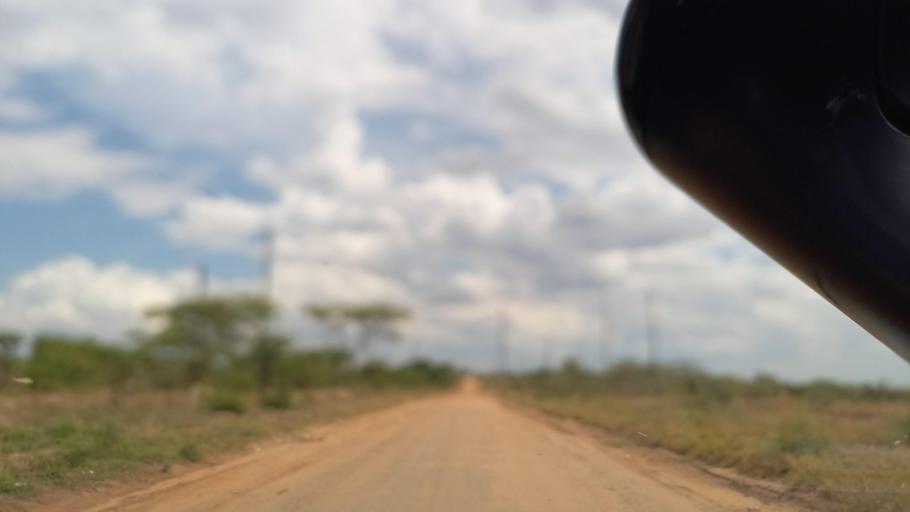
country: ZM
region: Southern
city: Nakambala
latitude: -16.0309
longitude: 27.9687
